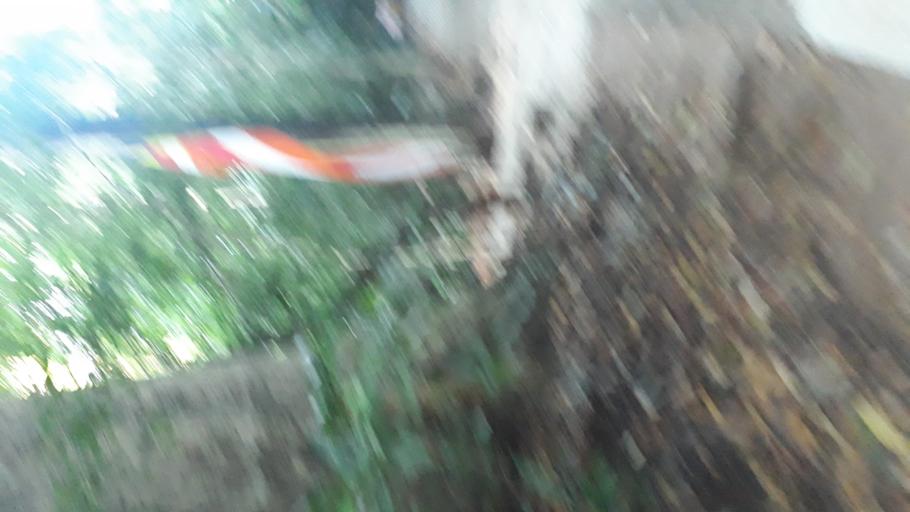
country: LK
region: Central
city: Dambulla
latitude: 7.7390
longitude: 80.5169
